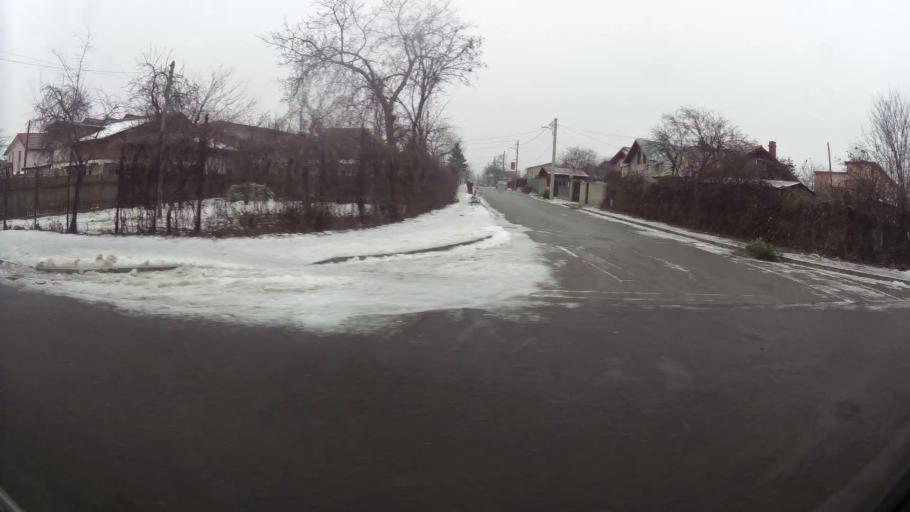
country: RO
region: Prahova
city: Ploiesti
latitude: 44.9538
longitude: 26.0429
